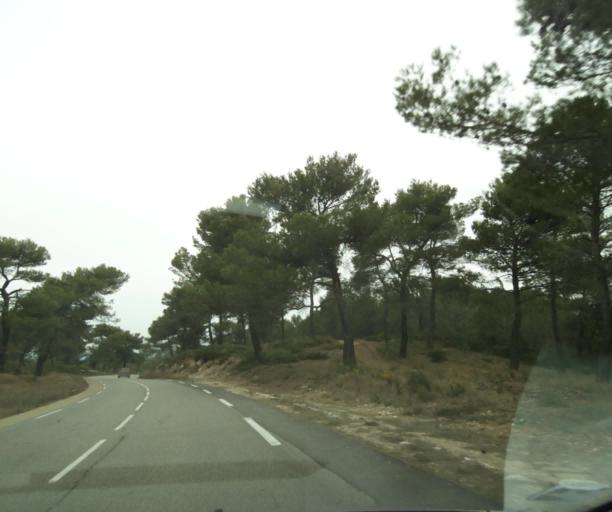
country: FR
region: Provence-Alpes-Cote d'Azur
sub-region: Departement des Bouches-du-Rhone
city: Belcodene
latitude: 43.4227
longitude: 5.6177
